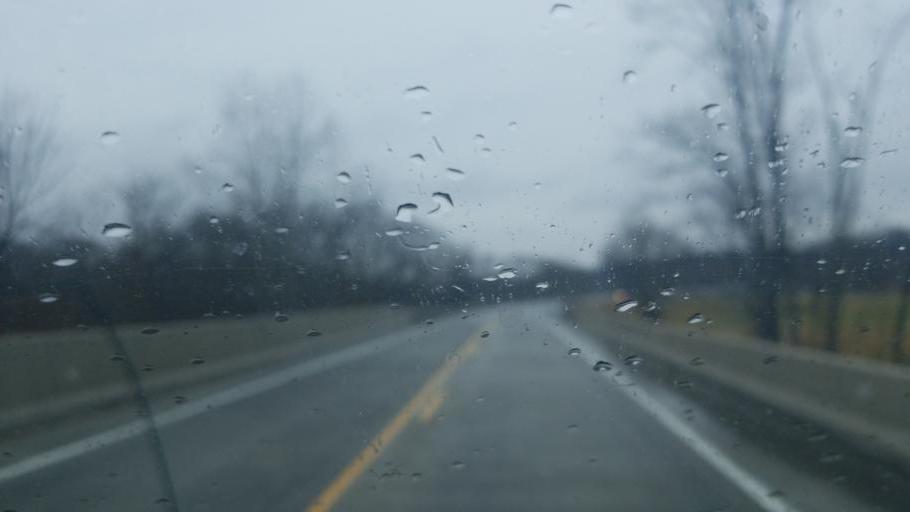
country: US
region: Indiana
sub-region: Brown County
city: Nashville
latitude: 39.1917
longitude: -86.1962
